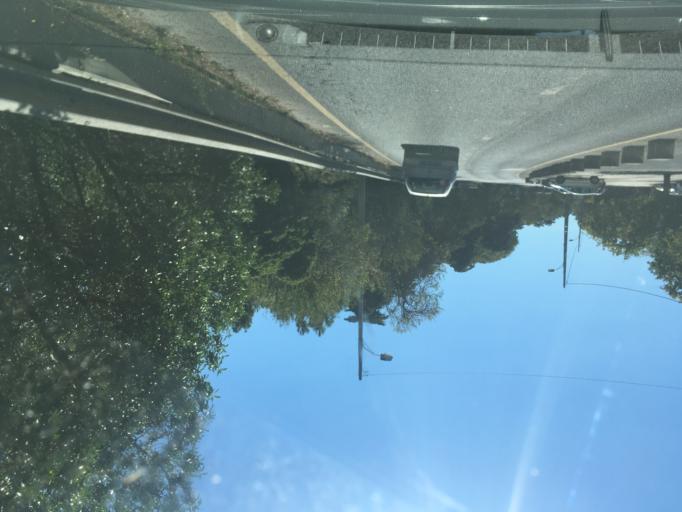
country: PT
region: Lisbon
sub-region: Oeiras
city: Alges
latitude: 38.7228
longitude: -9.1963
